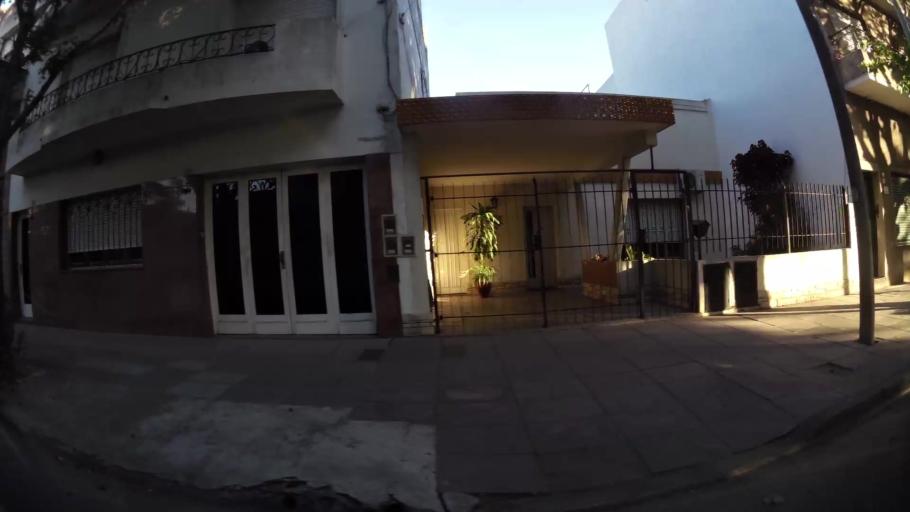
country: AR
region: Buenos Aires
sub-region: Partido de General San Martin
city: General San Martin
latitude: -34.5674
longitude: -58.5439
